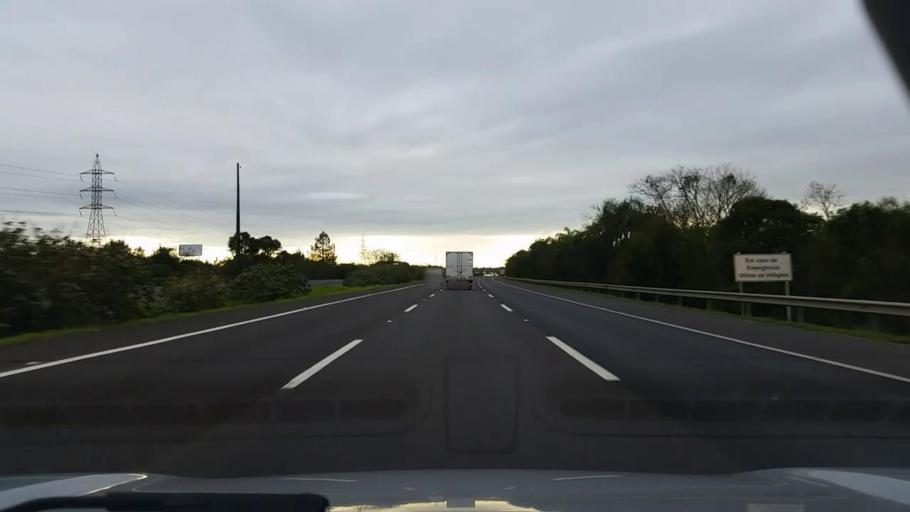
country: BR
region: Rio Grande do Sul
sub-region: Gravatai
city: Gravatai
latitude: -29.9535
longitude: -50.9958
